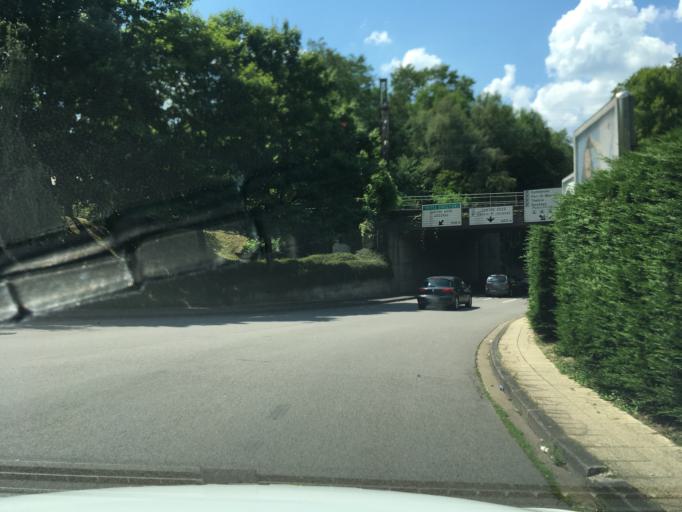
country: FR
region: Lorraine
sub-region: Departement de la Moselle
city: Metz
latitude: 49.1193
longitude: 6.1882
